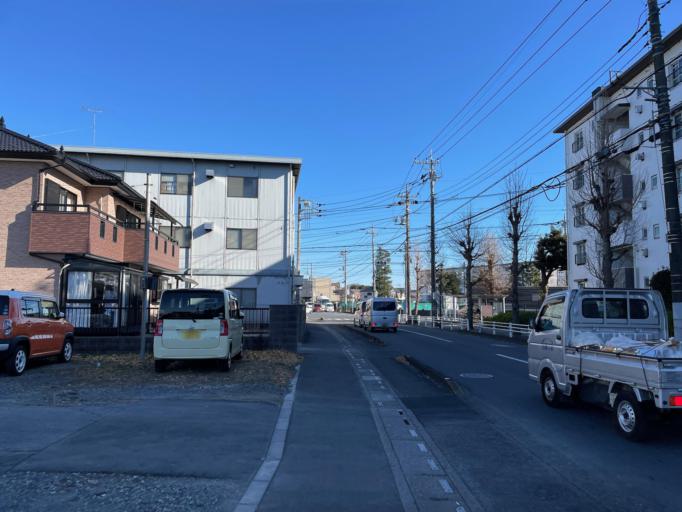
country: JP
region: Saitama
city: Ageoshimo
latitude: 35.9665
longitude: 139.6316
